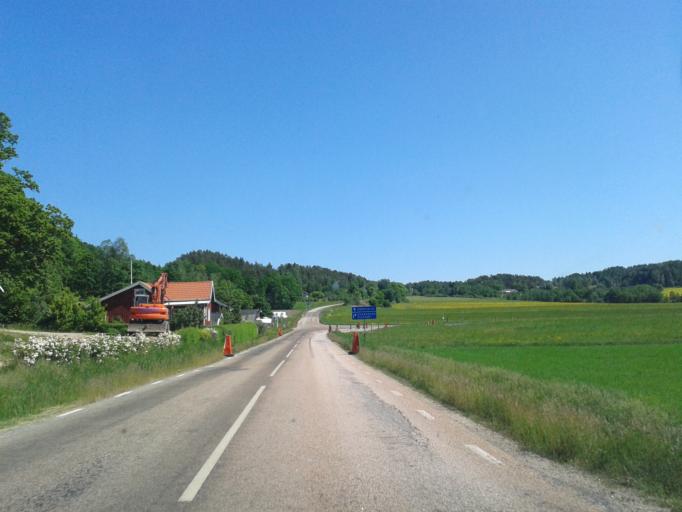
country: SE
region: Vaestra Goetaland
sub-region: Orust
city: Henan
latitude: 58.2587
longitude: 11.7304
